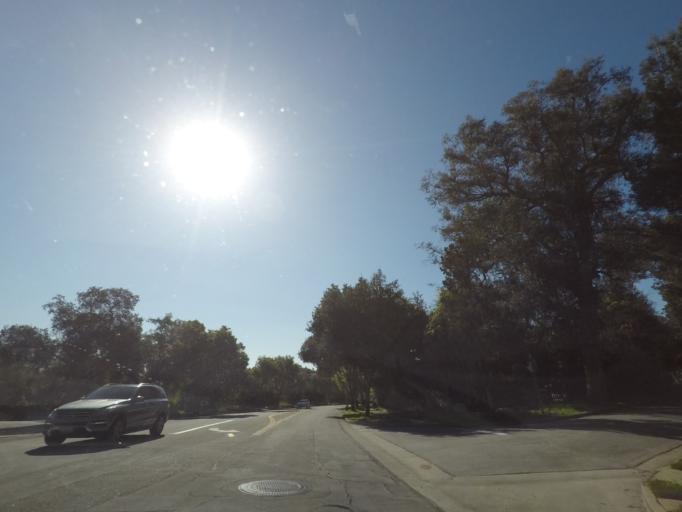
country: US
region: California
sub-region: Los Angeles County
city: Pasadena
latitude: 34.1530
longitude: -118.1682
